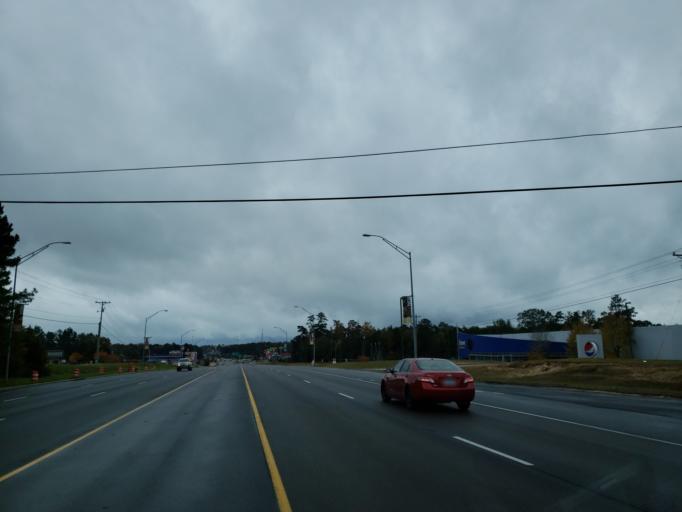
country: US
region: Mississippi
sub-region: Forrest County
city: Rawls Springs
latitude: 31.3649
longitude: -89.3540
